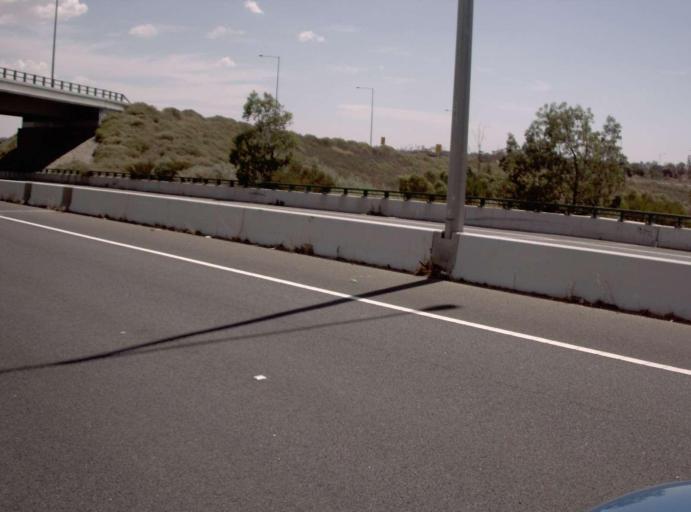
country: AU
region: Victoria
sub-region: Darebin
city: Reservoir
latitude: -37.6894
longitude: 144.9861
